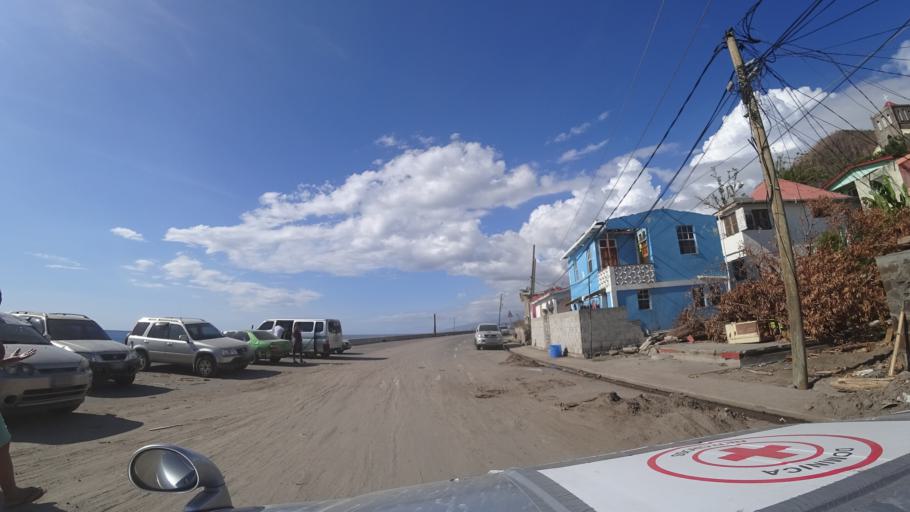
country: DM
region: Saint Luke
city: Pointe Michel
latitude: 15.2591
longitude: -61.3776
